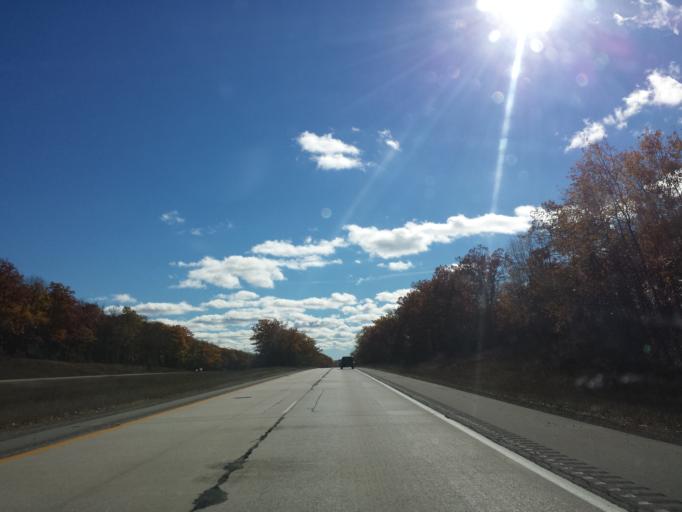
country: US
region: Michigan
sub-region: Cheboygan County
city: Indian River
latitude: 45.4944
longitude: -84.6160
